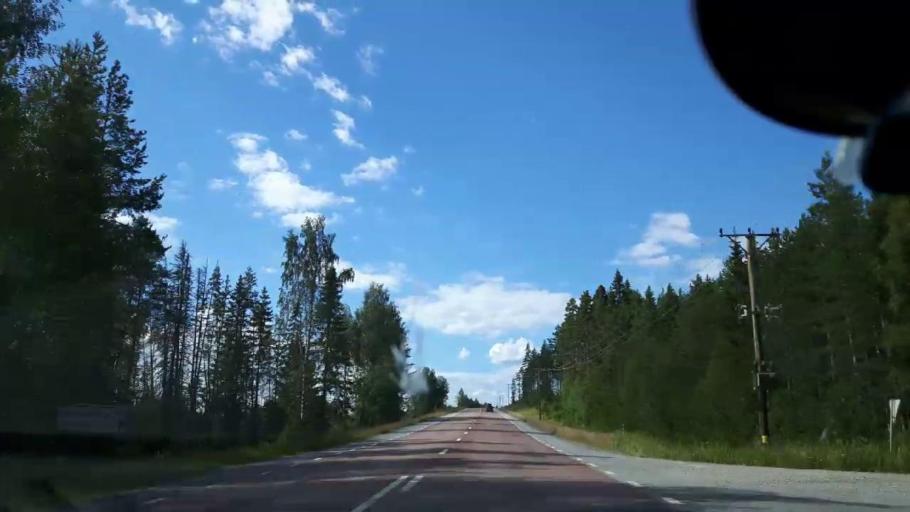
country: SE
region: Jaemtland
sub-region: Braecke Kommun
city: Braecke
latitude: 62.7740
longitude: 15.3977
